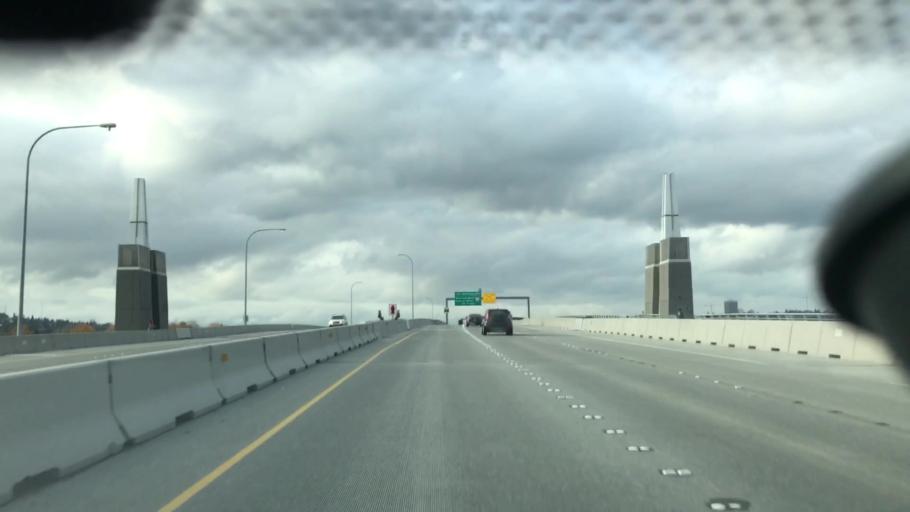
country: US
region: Washington
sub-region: King County
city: Medina
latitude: 47.6434
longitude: -122.2734
